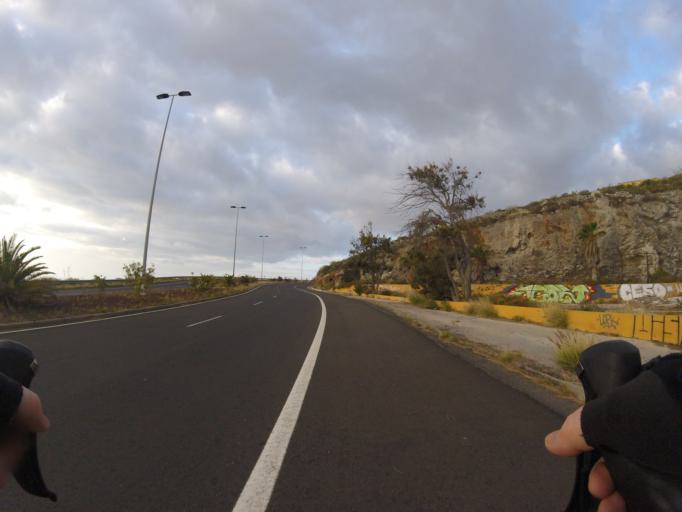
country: ES
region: Canary Islands
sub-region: Provincia de Santa Cruz de Tenerife
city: La Laguna
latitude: 28.4310
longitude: -16.3121
